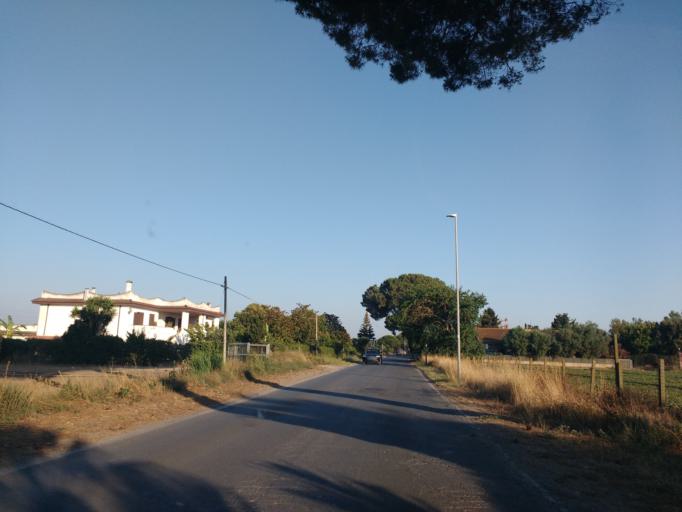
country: IT
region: Latium
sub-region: Citta metropolitana di Roma Capitale
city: Maccarese
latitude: 41.8580
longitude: 12.2150
